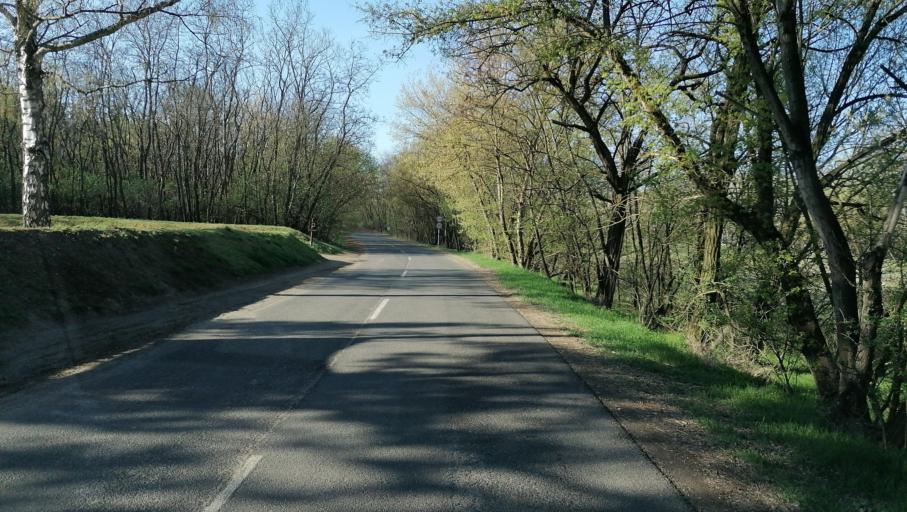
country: HU
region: Pest
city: Szentendre
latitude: 47.6724
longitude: 19.0873
